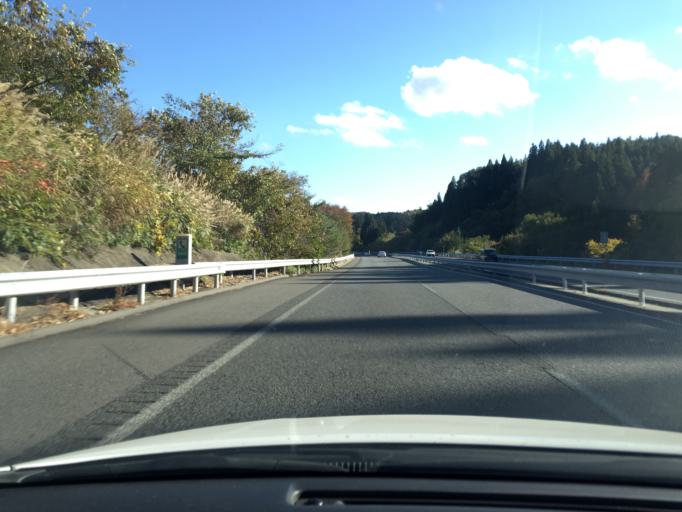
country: JP
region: Fukushima
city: Funehikimachi-funehiki
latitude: 37.2603
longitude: 140.6482
